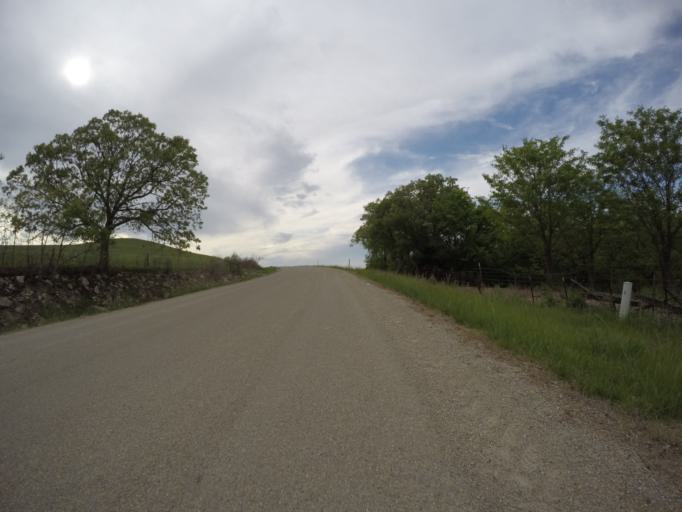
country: US
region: Kansas
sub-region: Riley County
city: Ogden
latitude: 39.0295
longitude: -96.6129
